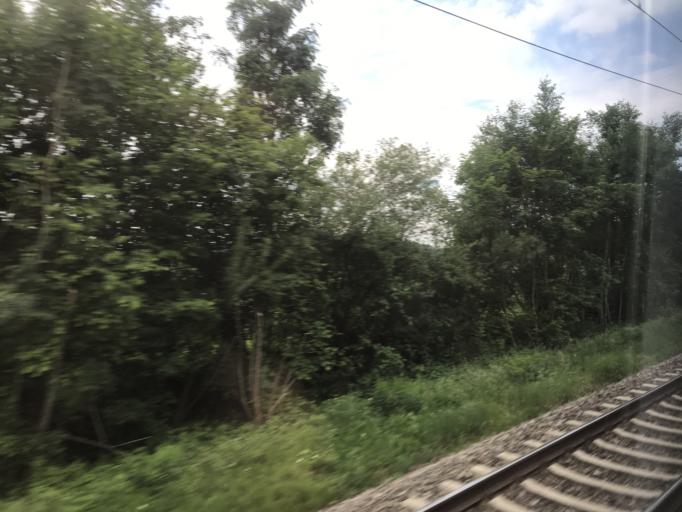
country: DE
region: Bavaria
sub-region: Swabia
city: Nersingen
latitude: 48.4245
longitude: 10.1043
